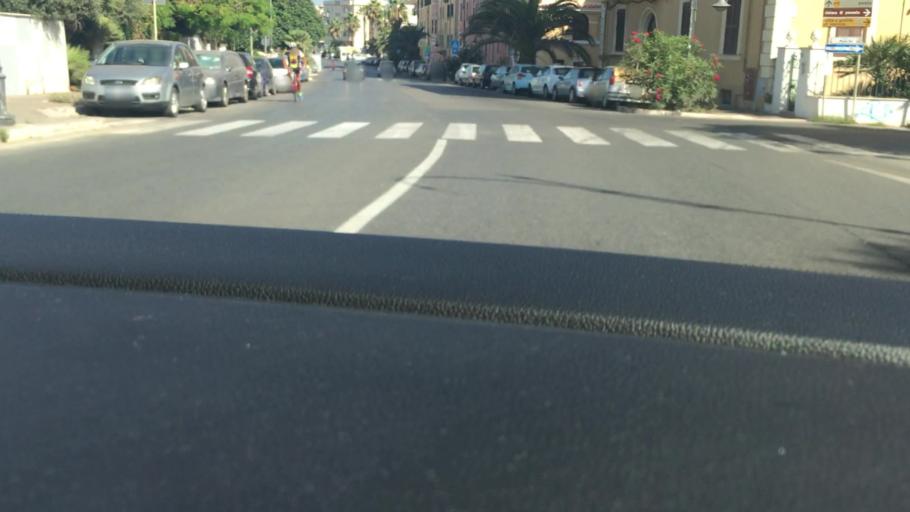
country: IT
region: Latium
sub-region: Citta metropolitana di Roma Capitale
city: Anzio
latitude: 41.4460
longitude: 12.6224
